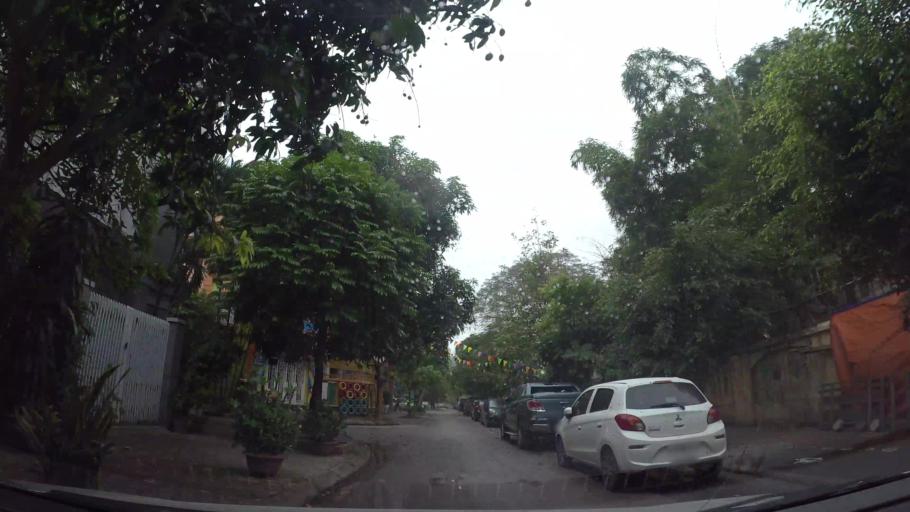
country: VN
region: Ha Noi
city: Cau Giay
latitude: 21.0140
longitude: 105.7983
